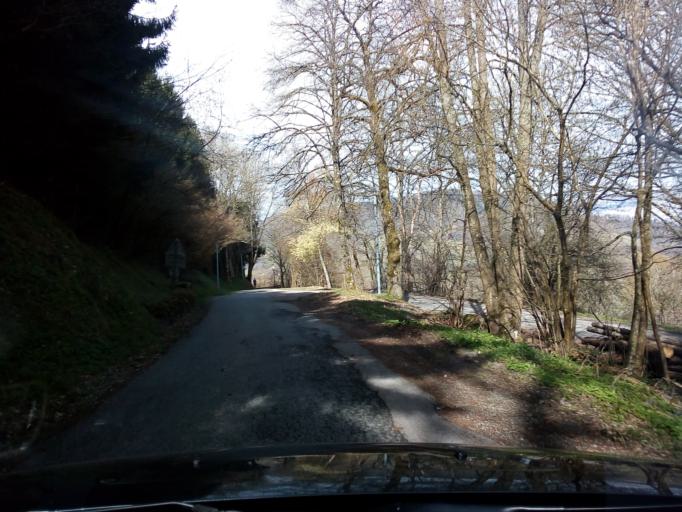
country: FR
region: Rhone-Alpes
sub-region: Departement de l'Isere
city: Revel
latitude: 45.1659
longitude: 5.8619
